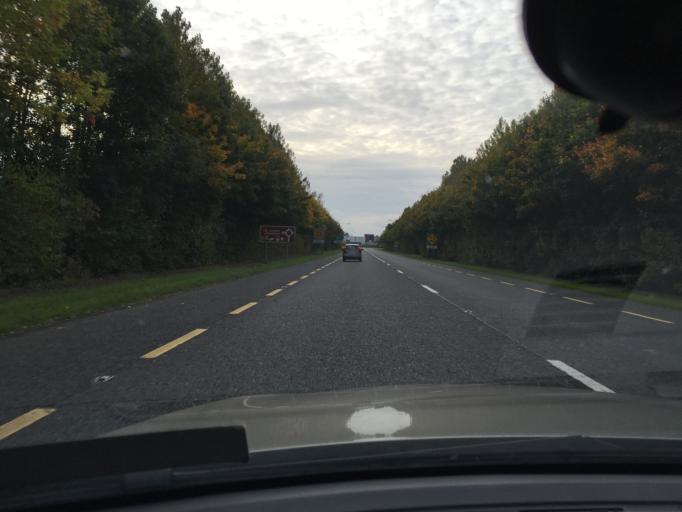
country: IE
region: Leinster
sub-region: An Longfort
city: Longford
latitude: 53.7418
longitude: -7.7957
